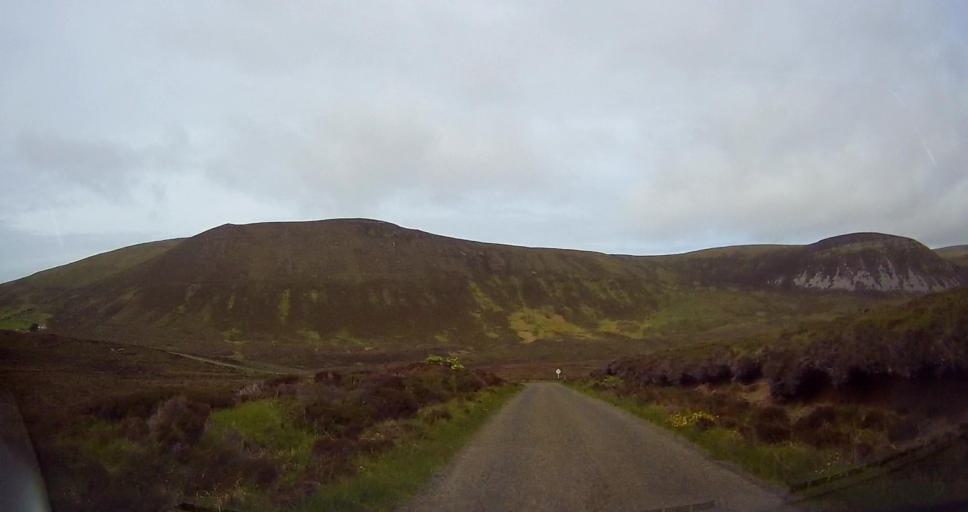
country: GB
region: Scotland
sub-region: Orkney Islands
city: Stromness
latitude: 58.8822
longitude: -3.3775
